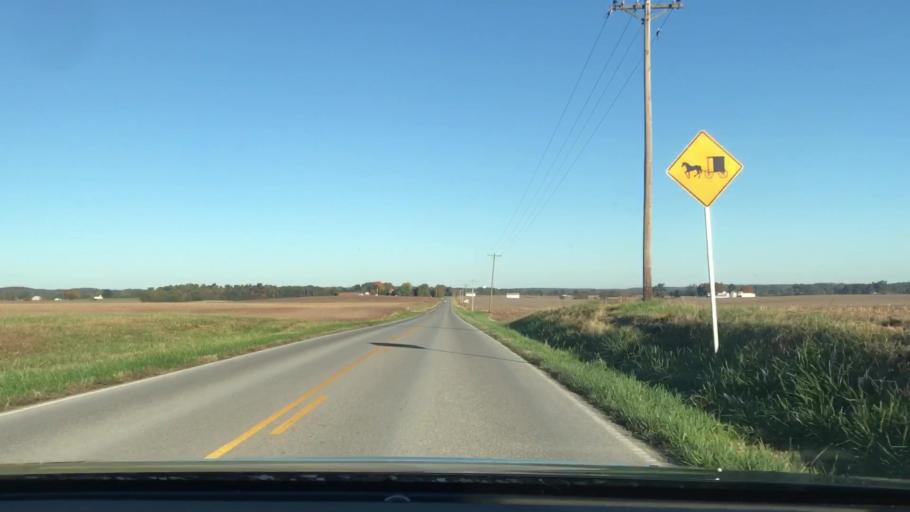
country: US
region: Kentucky
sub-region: Logan County
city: Auburn
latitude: 36.8327
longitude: -86.6852
